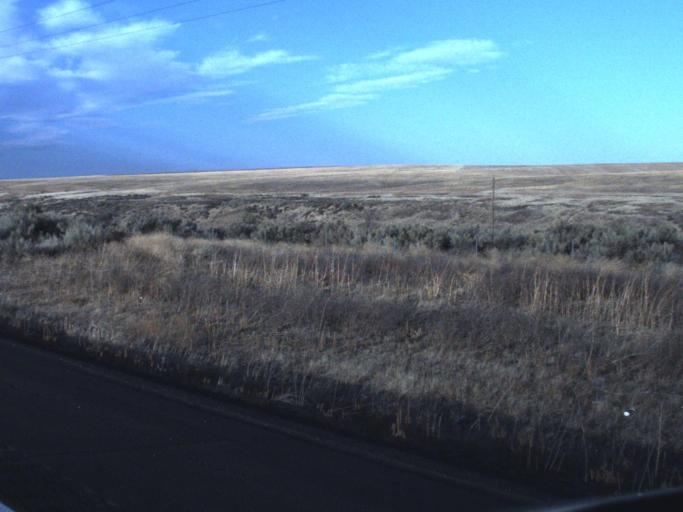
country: US
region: Washington
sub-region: Adams County
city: Ritzville
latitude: 47.0441
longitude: -118.4468
